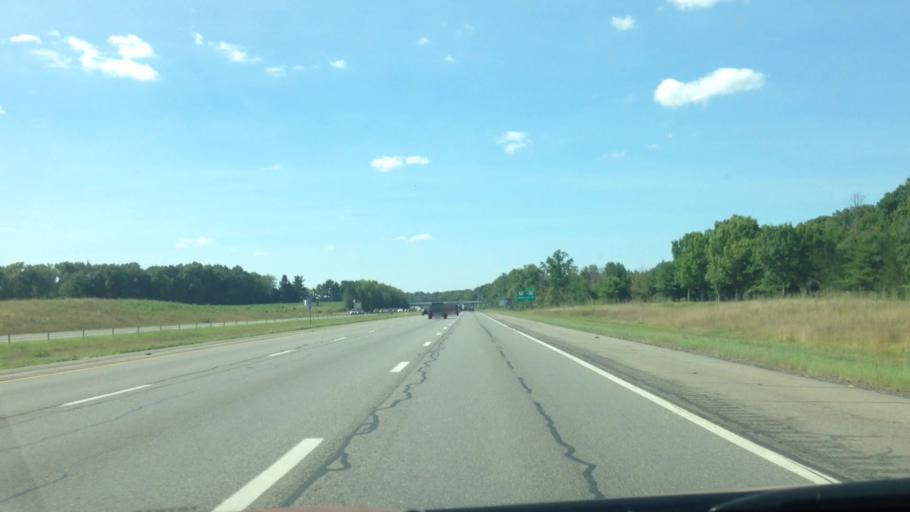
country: US
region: Ohio
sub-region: Summit County
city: Greensburg
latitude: 40.9493
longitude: -81.4501
